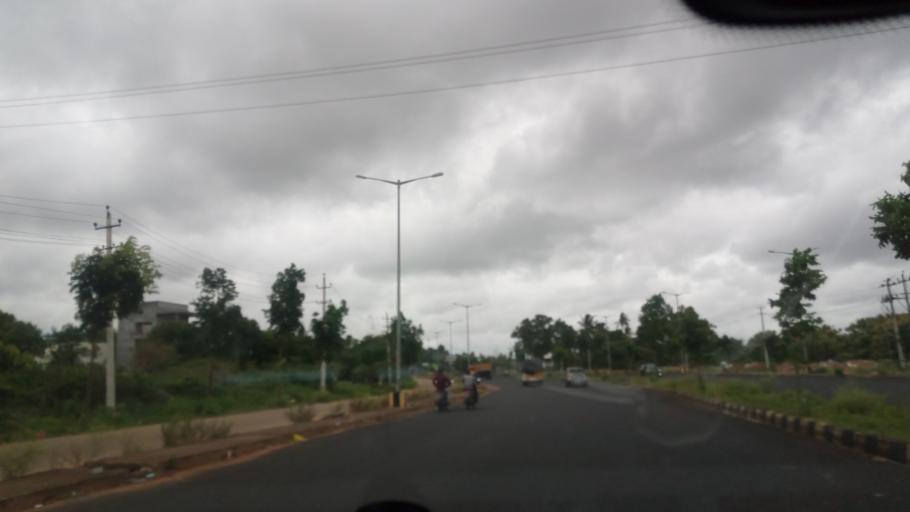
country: IN
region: Karnataka
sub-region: Mysore
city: Mysore
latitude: 12.2990
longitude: 76.6030
